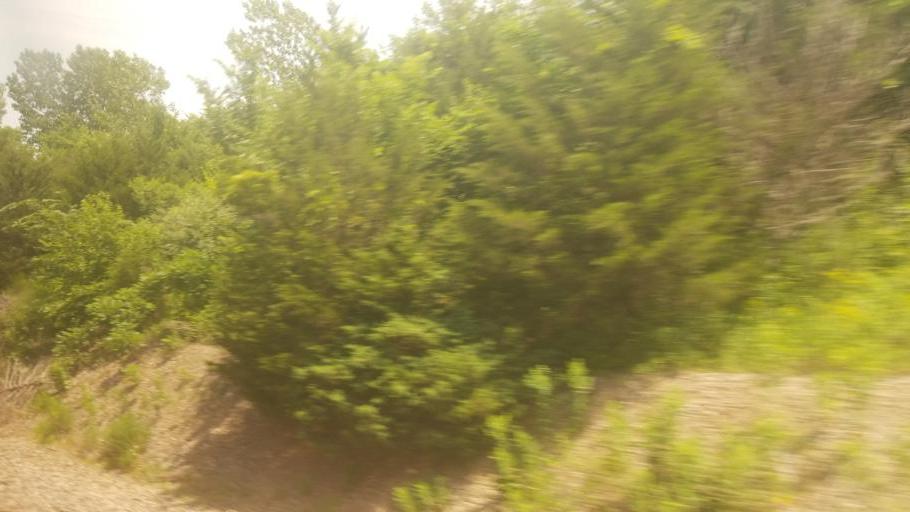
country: US
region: Missouri
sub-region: Macon County
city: La Plata
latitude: 40.0655
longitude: -92.4583
